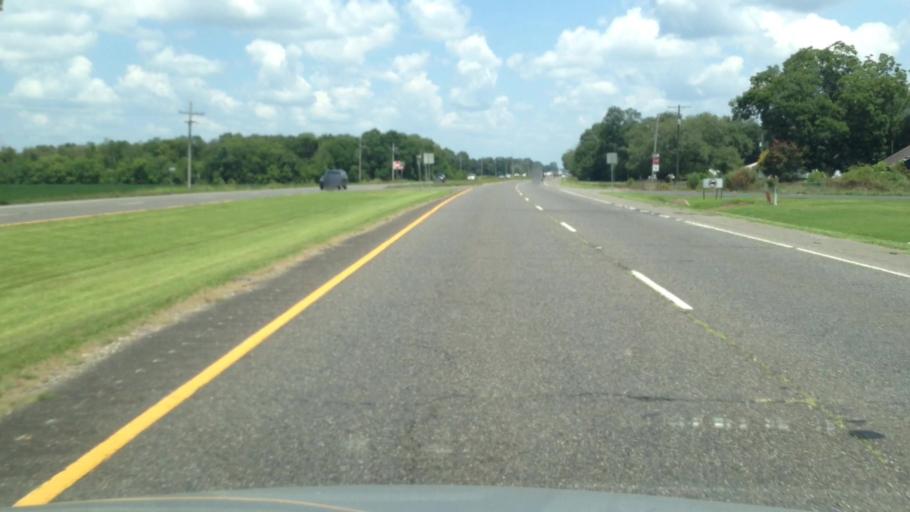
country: US
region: Louisiana
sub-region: Saint Landry Parish
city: Port Barre
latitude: 30.5478
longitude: -91.9865
